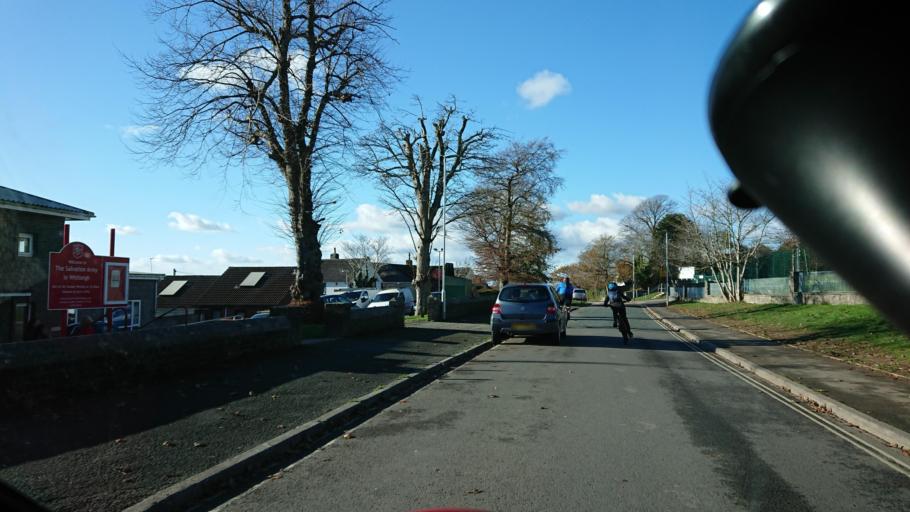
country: GB
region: England
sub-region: Plymouth
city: Plymouth
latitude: 50.4173
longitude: -4.1430
